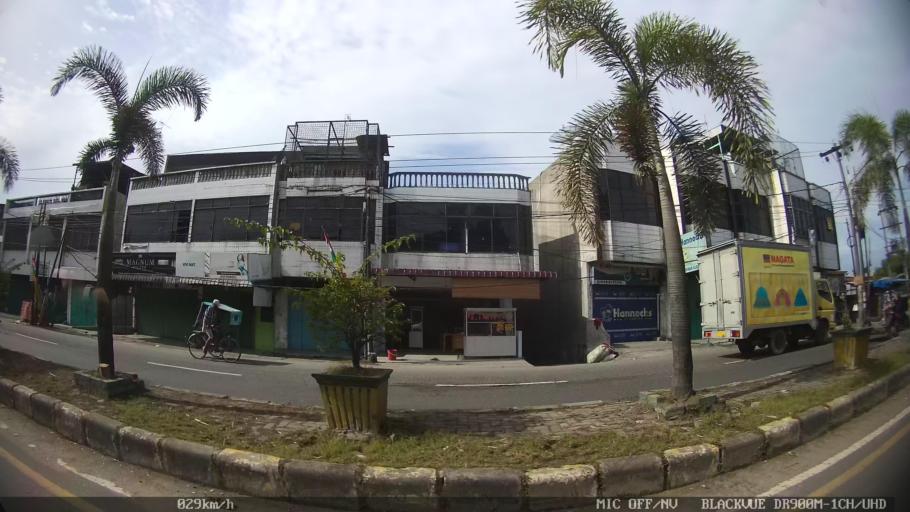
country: ID
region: North Sumatra
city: Medan
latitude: 3.6249
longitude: 98.6655
